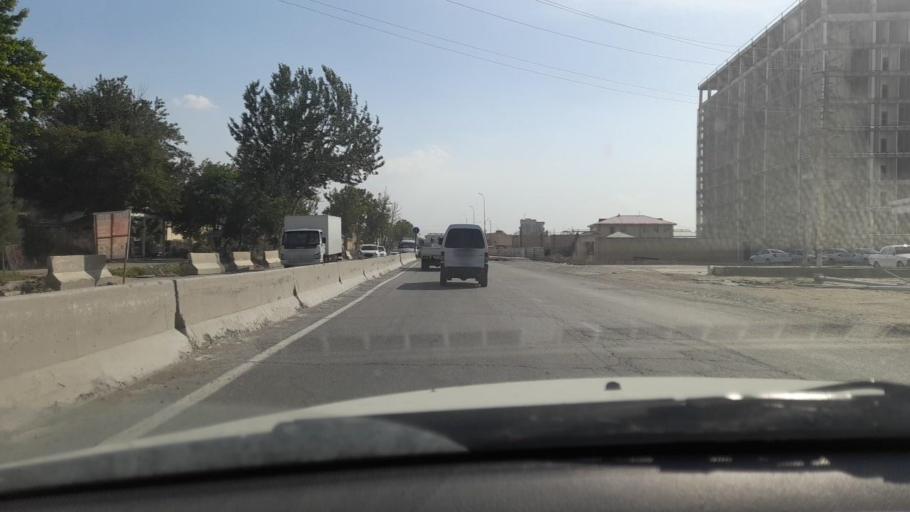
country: UZ
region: Samarqand
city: Samarqand
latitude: 39.6884
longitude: 67.0094
